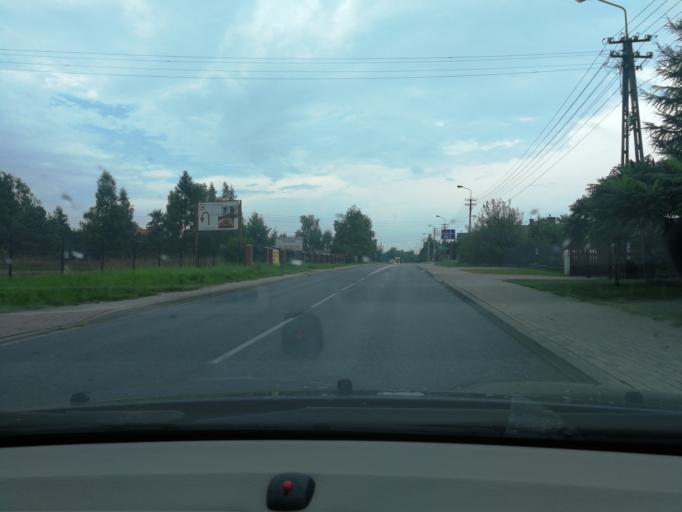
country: PL
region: Masovian Voivodeship
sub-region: Powiat zyrardowski
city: Radziejowice
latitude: 52.0076
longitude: 20.5576
